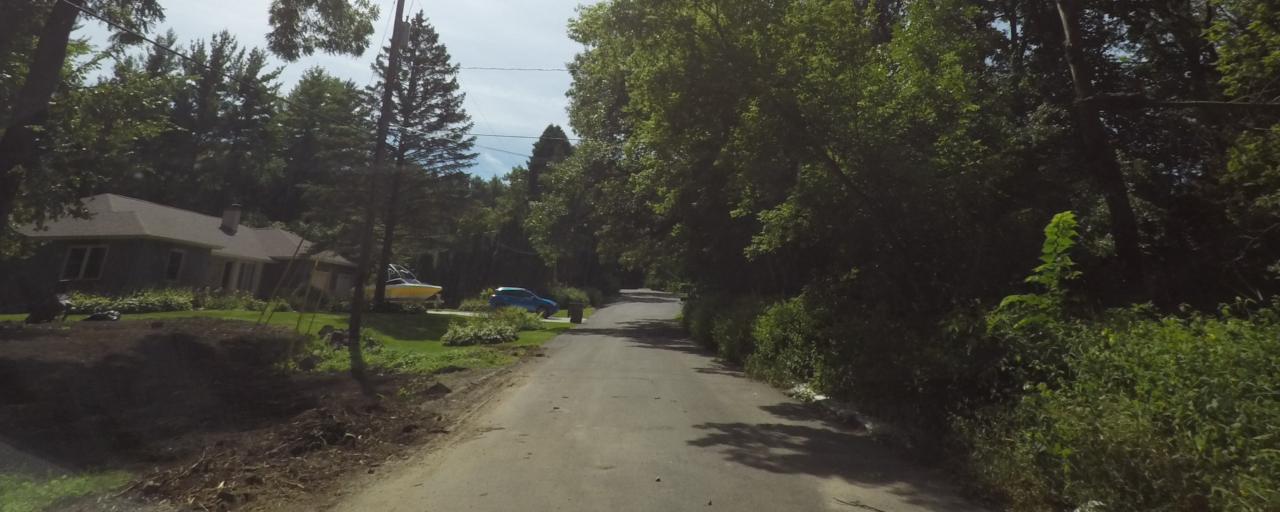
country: US
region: Wisconsin
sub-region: Dane County
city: Middleton
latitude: 43.0847
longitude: -89.4802
